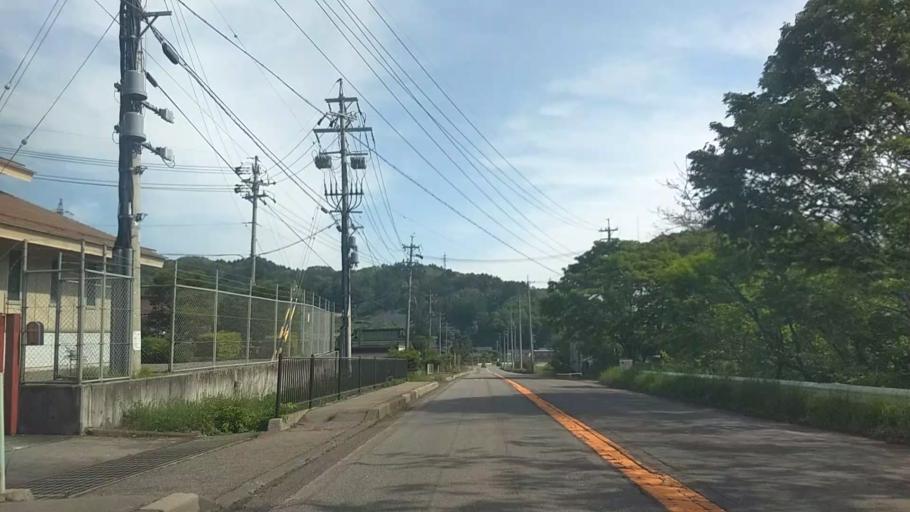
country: JP
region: Nagano
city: Saku
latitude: 36.0560
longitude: 138.4670
